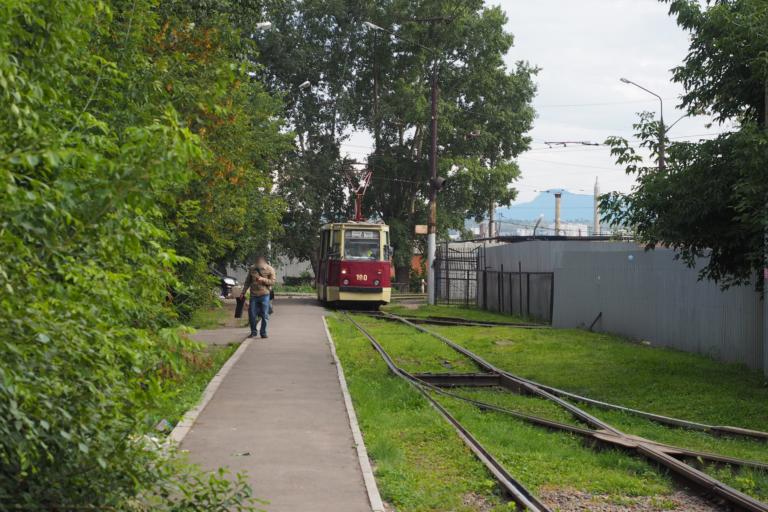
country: RU
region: Krasnoyarskiy
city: Berezovka
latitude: 56.0257
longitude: 93.0226
